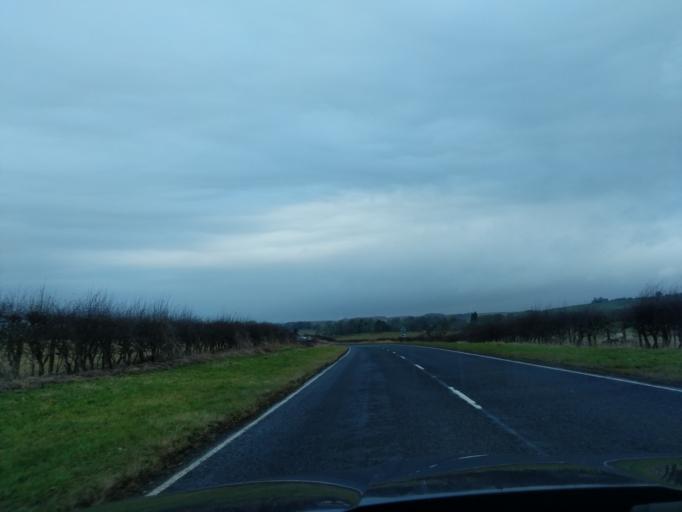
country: GB
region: England
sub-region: Northumberland
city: Rothley
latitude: 55.1484
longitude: -1.9976
